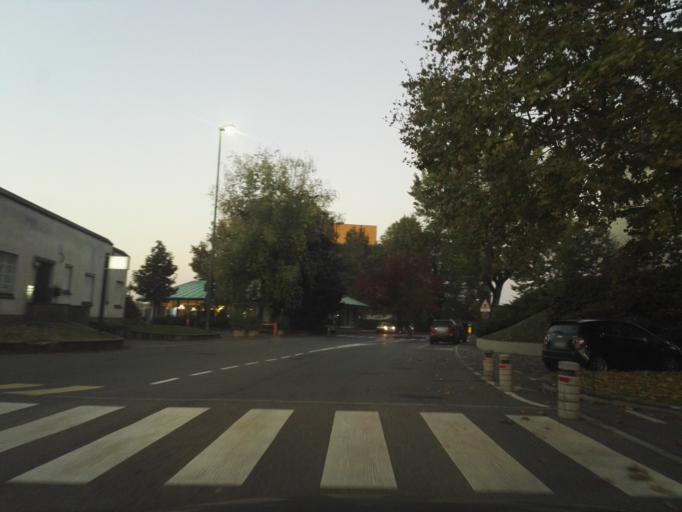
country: IT
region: Lombardy
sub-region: Citta metropolitana di Milano
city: San Bovio-San Felice
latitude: 45.4736
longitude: 9.3048
